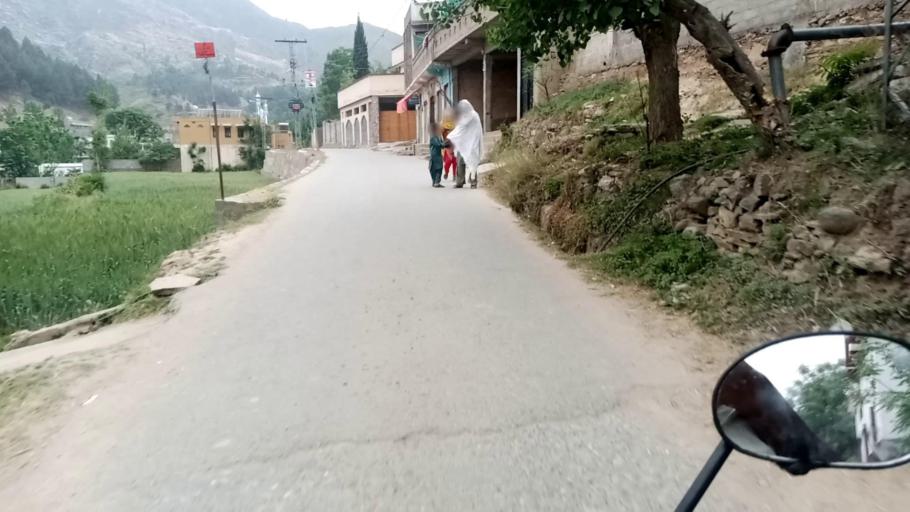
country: PK
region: Khyber Pakhtunkhwa
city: Saidu Sharif
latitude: 34.7539
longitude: 72.3782
